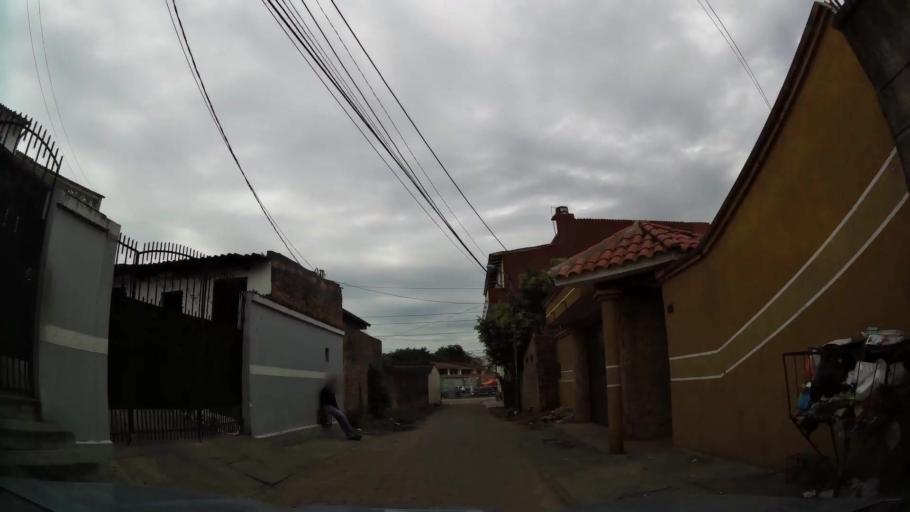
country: BO
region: Santa Cruz
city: Santa Cruz de la Sierra
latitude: -17.7769
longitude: -63.2041
